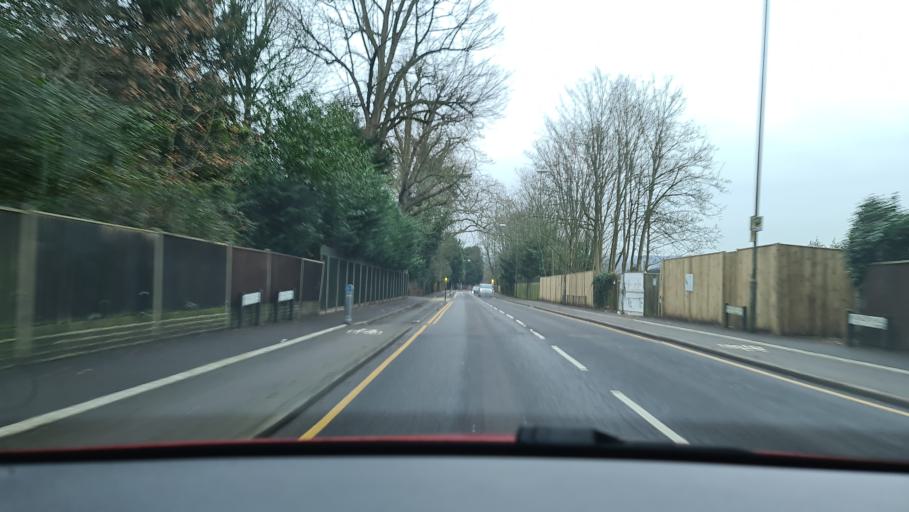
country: GB
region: England
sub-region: Greater London
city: New Malden
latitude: 51.4308
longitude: -0.2658
